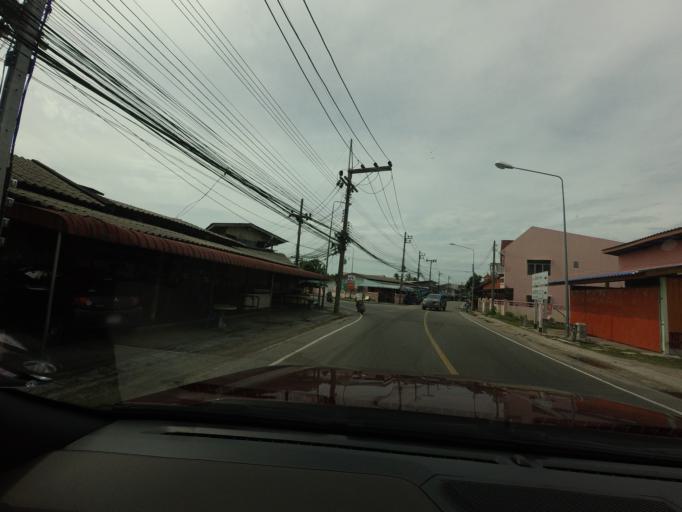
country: TH
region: Narathiwat
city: Tak Bai
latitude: 6.2376
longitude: 102.0874
